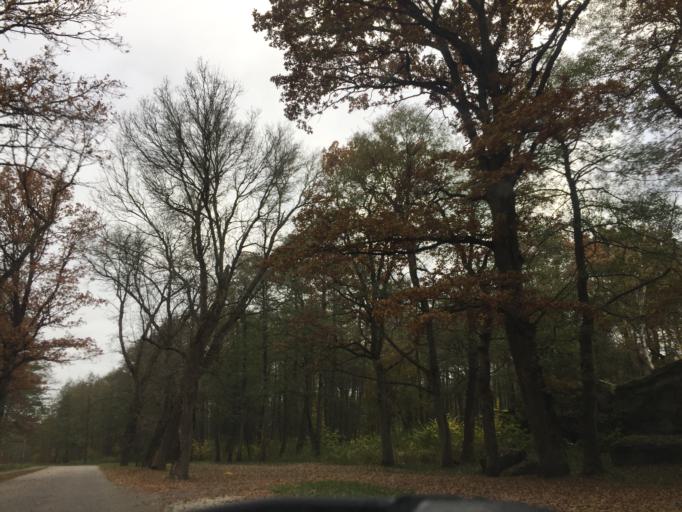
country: LV
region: Liepaja
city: Vec-Liepaja
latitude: 56.5452
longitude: 21.0793
